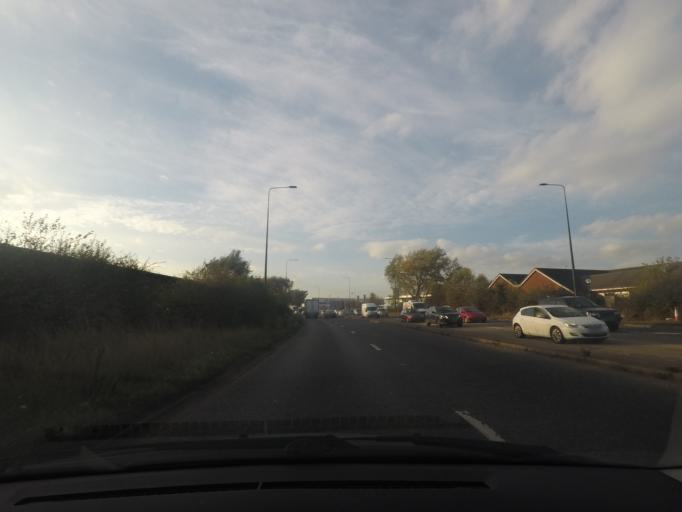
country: GB
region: England
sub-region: North East Lincolnshire
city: Grimbsy
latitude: 53.5757
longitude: -0.0975
